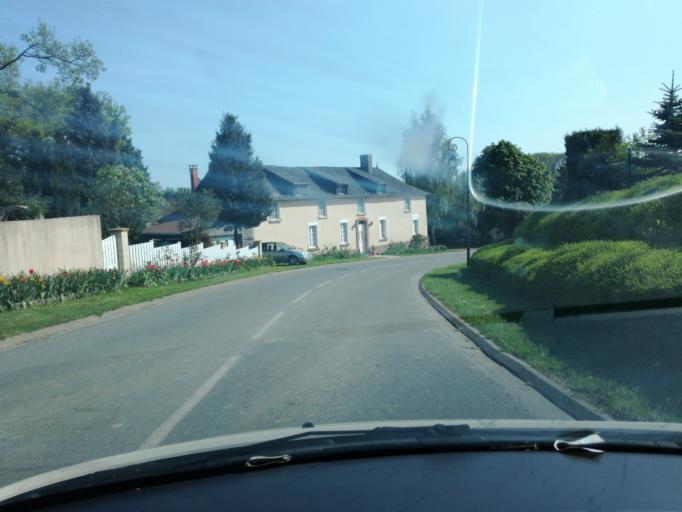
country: FR
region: Picardie
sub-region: Departement de la Somme
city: Poix-de-Picardie
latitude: 49.8214
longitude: 2.0201
